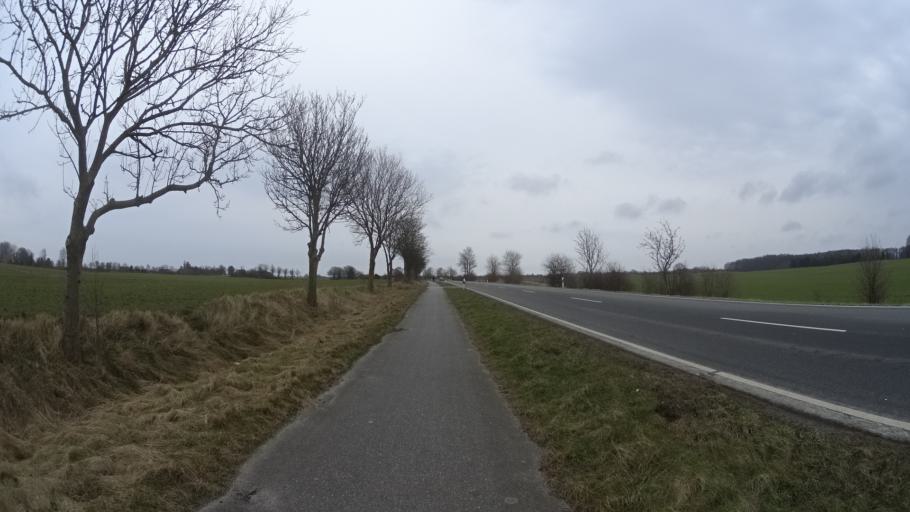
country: DE
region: Schleswig-Holstein
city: Stakendorf
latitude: 54.3784
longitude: 10.4550
